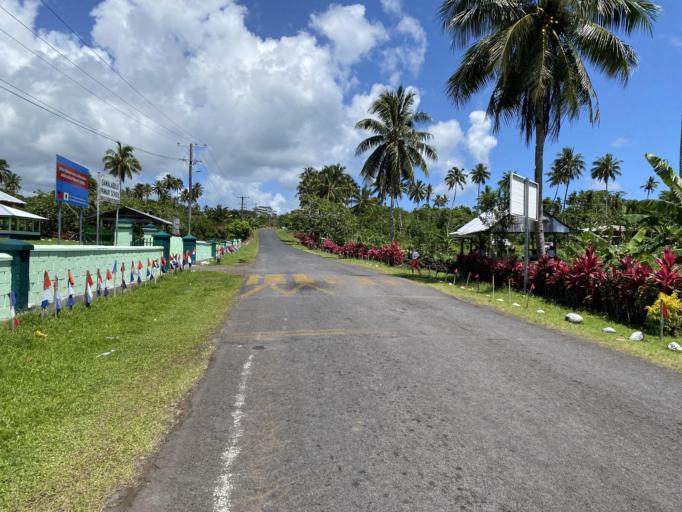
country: WS
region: Gagaifomauga
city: Safotu
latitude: -13.4988
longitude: -172.3050
